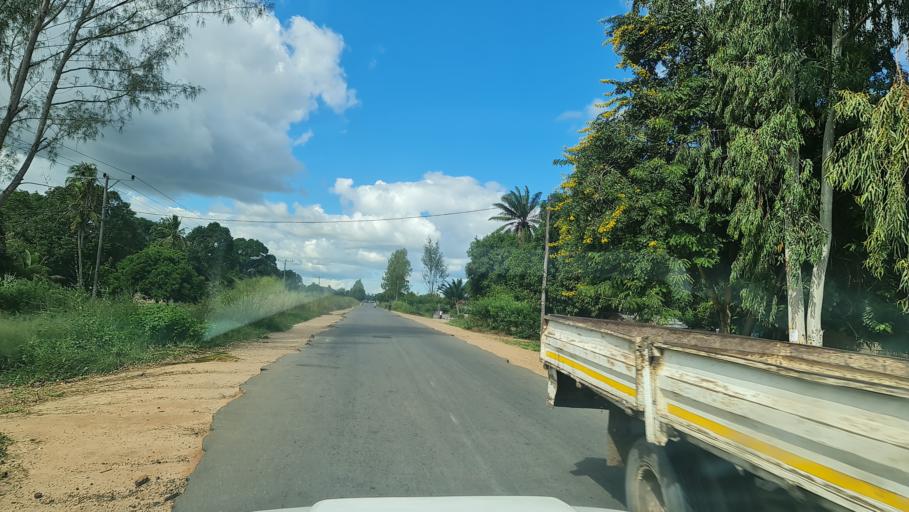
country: MZ
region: Zambezia
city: Quelimane
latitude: -17.5977
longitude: 36.7904
